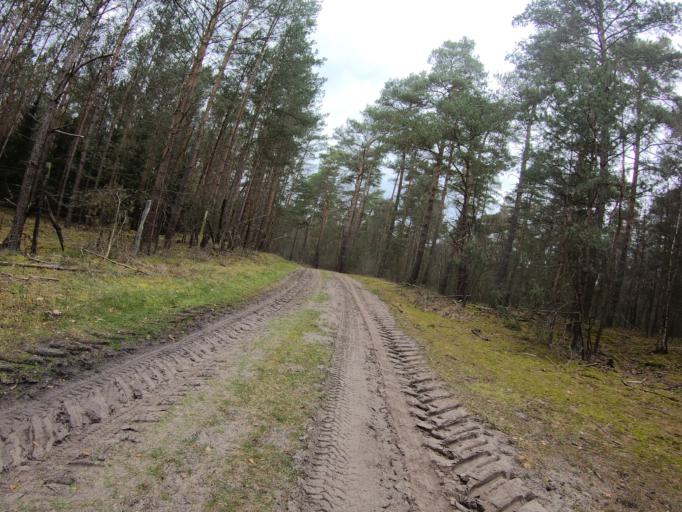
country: DE
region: Lower Saxony
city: Leiferde
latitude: 52.4862
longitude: 10.4485
